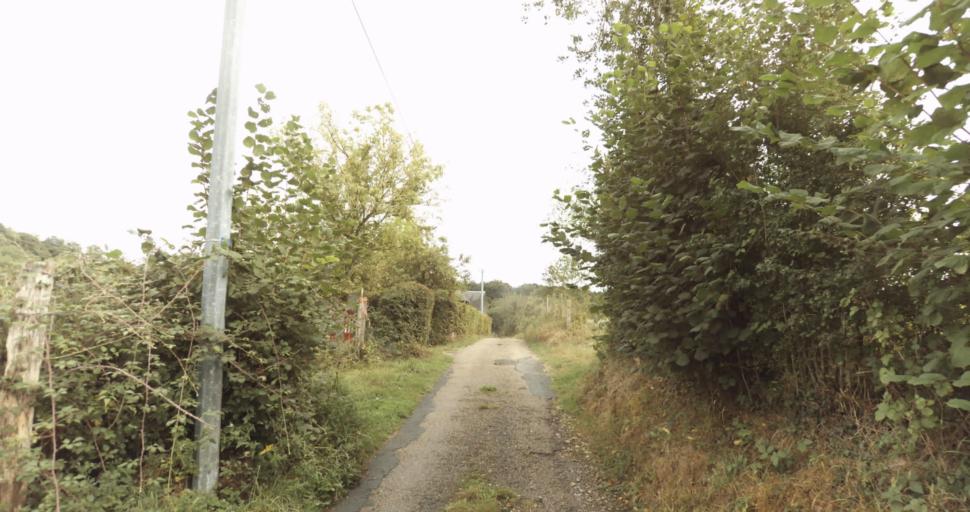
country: FR
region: Lower Normandy
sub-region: Departement de l'Orne
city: Vimoutiers
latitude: 48.8638
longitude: 0.1729
